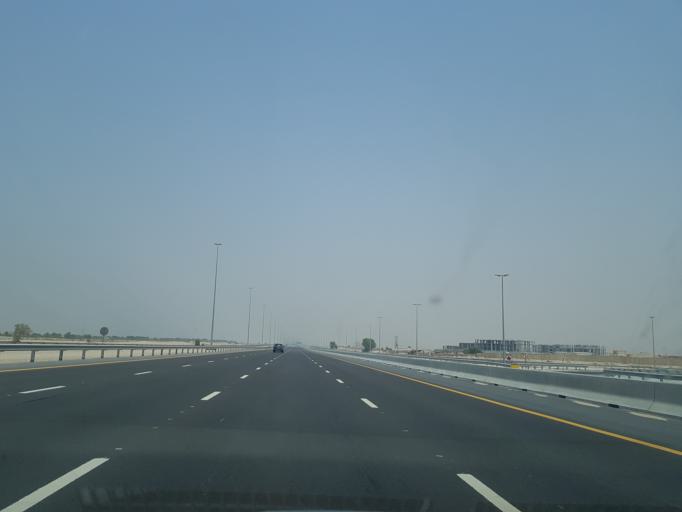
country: AE
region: Dubai
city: Dubai
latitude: 25.0431
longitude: 55.2744
